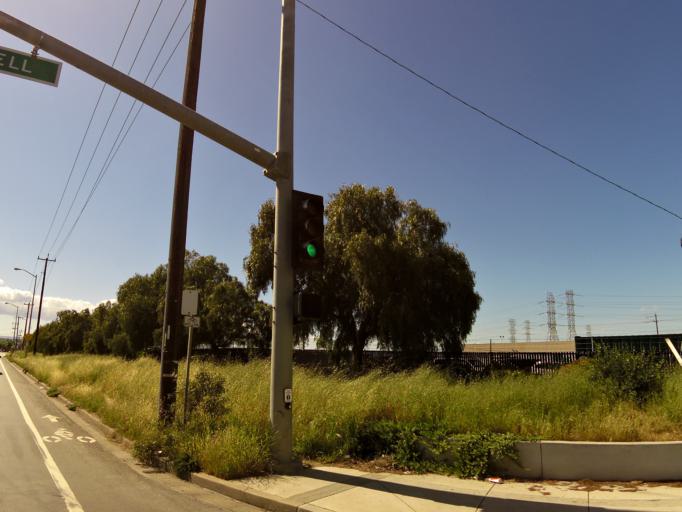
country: US
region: California
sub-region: Alameda County
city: Fremont
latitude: 37.5038
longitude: -121.9764
